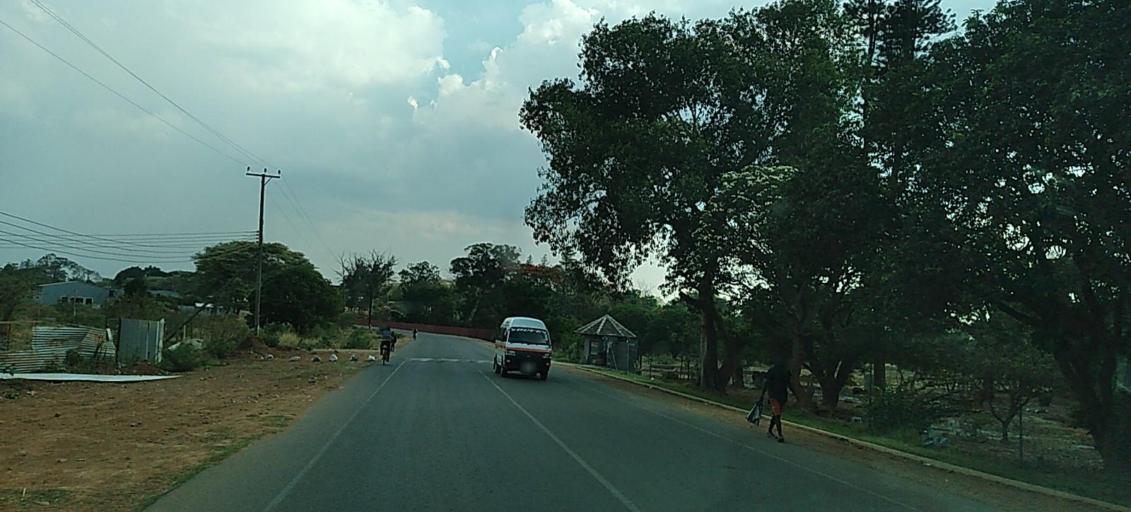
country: ZM
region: Lusaka
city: Lusaka
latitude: -15.5198
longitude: 28.2347
